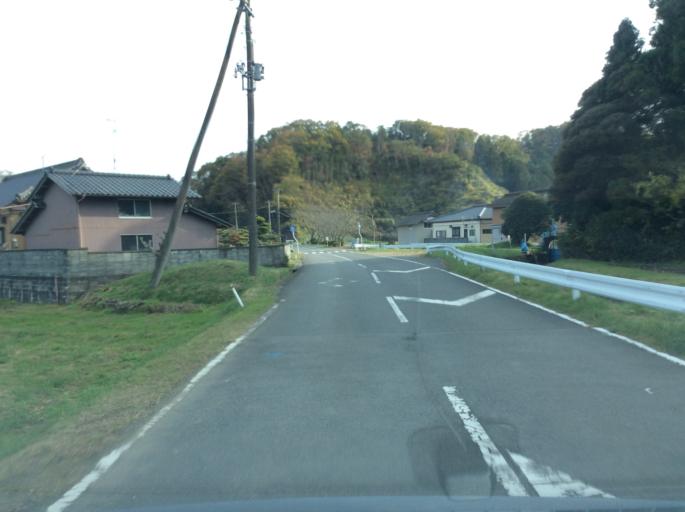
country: JP
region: Fukushima
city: Iwaki
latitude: 37.0896
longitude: 140.9414
